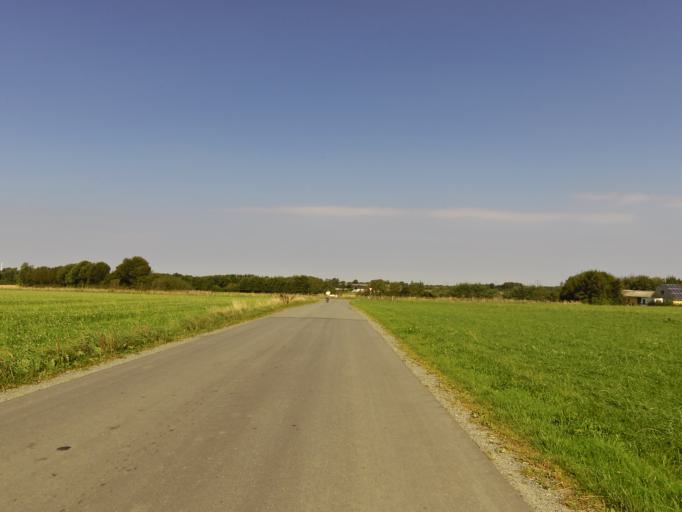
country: DK
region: South Denmark
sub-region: Vejen Kommune
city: Rodding
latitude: 55.3911
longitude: 9.1416
